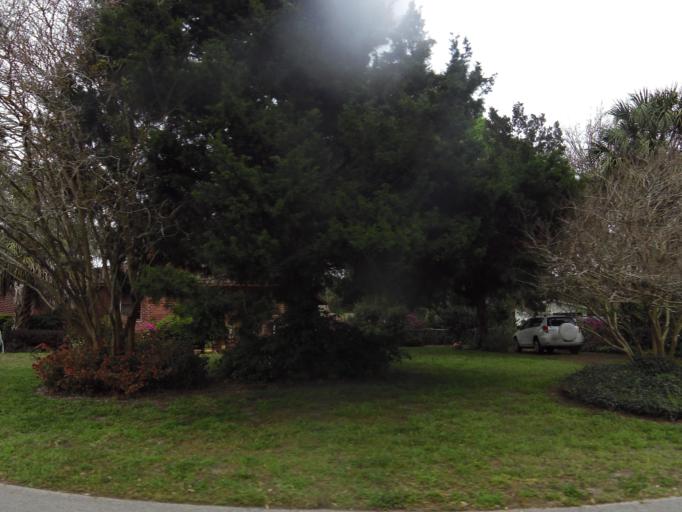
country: US
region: Florida
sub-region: Duval County
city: Jacksonville
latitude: 30.2797
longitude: -81.6568
